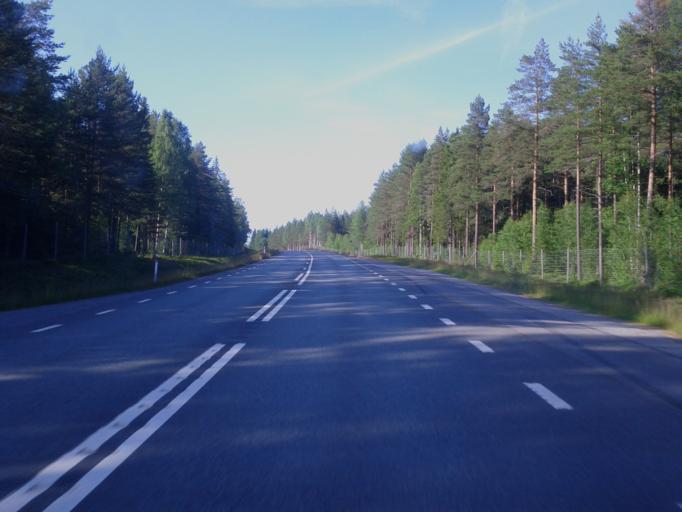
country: SE
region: Vaesterbotten
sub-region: Robertsfors Kommun
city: Robertsfors
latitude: 64.0225
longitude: 20.8400
